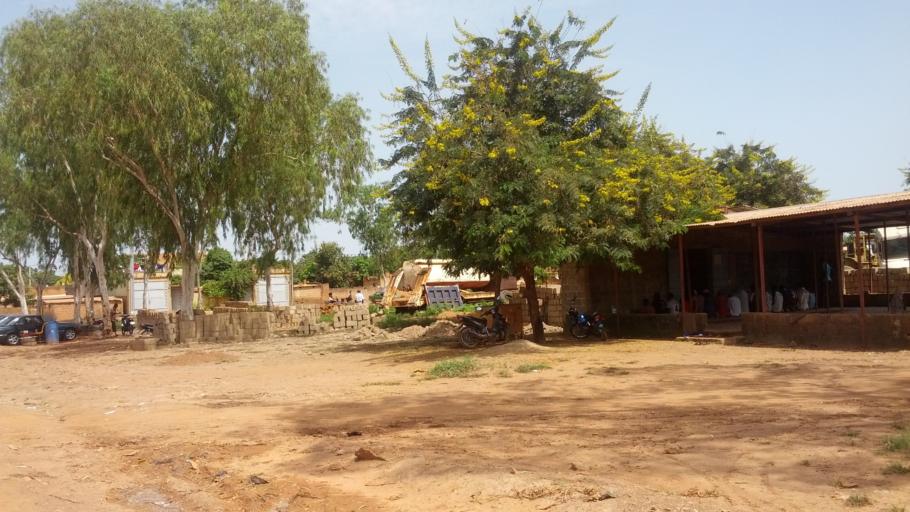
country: BF
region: Centre
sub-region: Kadiogo Province
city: Ouagadougou
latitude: 12.3854
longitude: -1.4669
